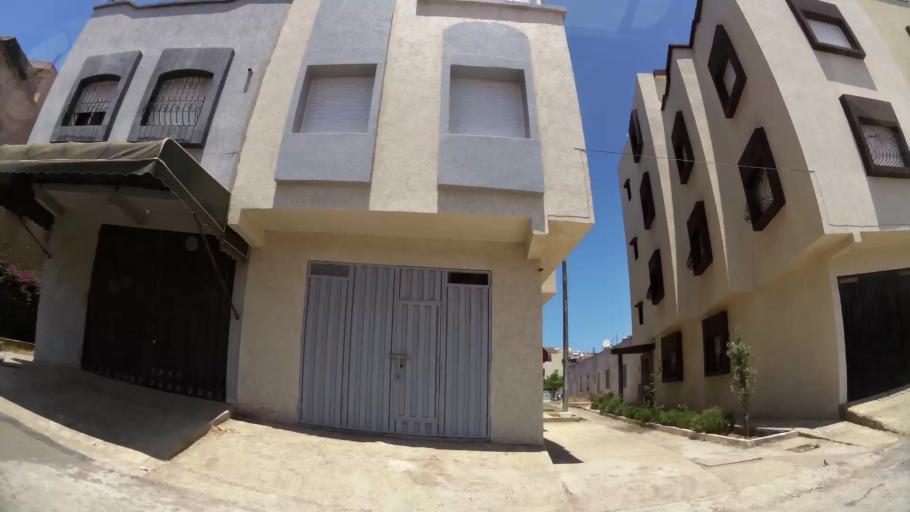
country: MA
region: Gharb-Chrarda-Beni Hssen
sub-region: Kenitra Province
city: Kenitra
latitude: 34.2540
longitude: -6.6201
